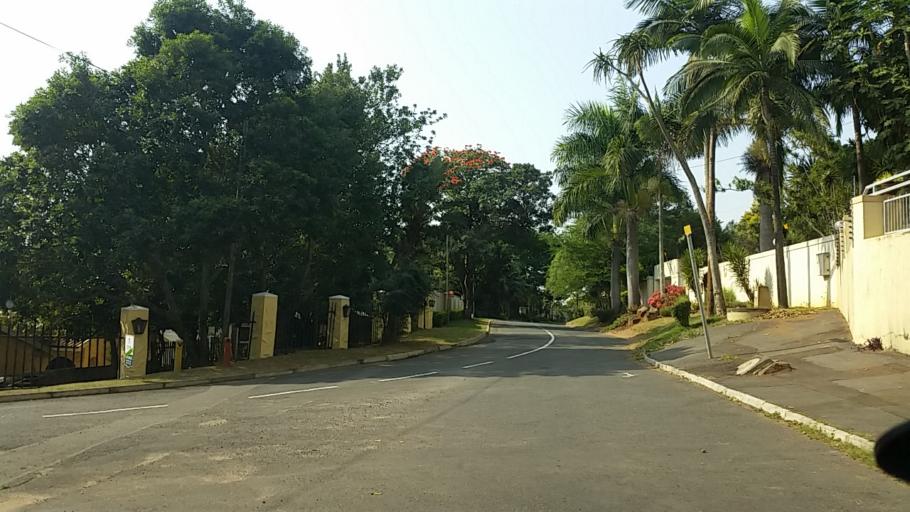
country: ZA
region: KwaZulu-Natal
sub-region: eThekwini Metropolitan Municipality
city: Berea
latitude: -29.8333
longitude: 30.9274
